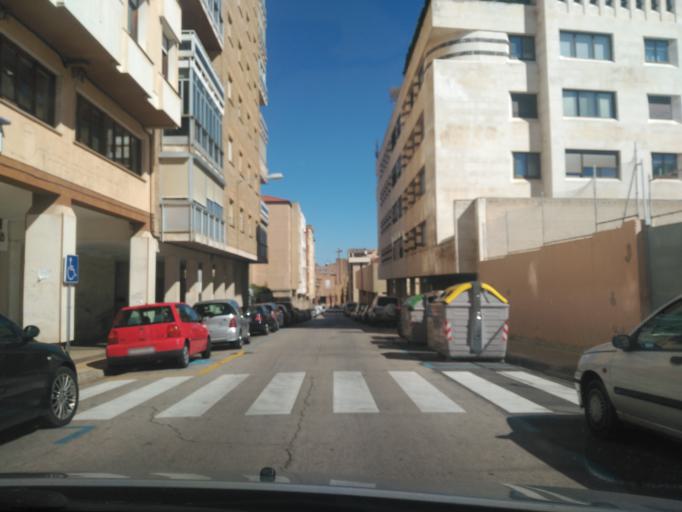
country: ES
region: Castille and Leon
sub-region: Provincia de Soria
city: Soria
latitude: 41.7653
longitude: -2.4715
